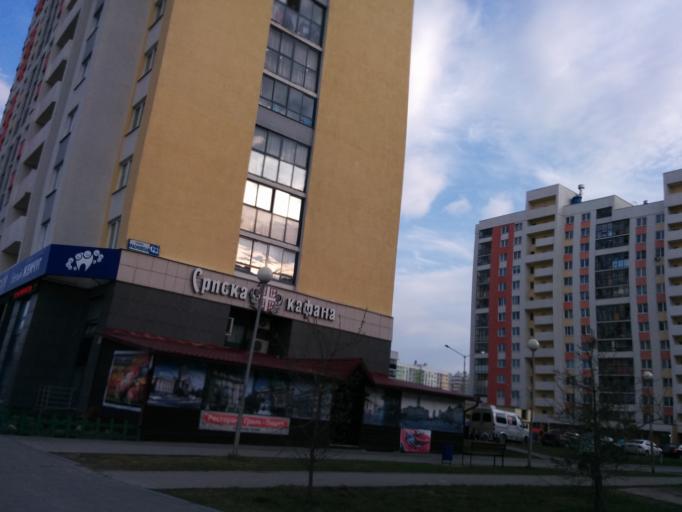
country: RU
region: Sverdlovsk
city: Sovkhoznyy
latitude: 56.7918
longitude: 60.5234
